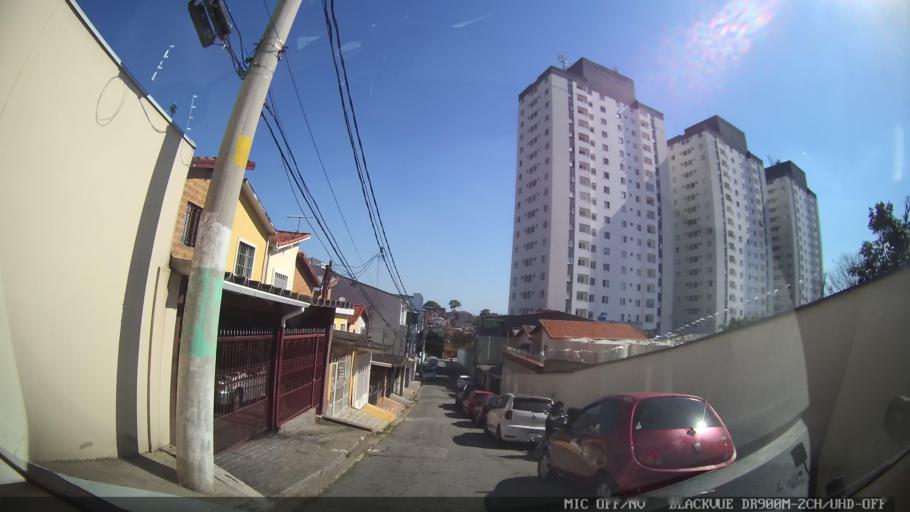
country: BR
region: Sao Paulo
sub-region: Sao Paulo
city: Sao Paulo
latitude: -23.4910
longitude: -46.6525
